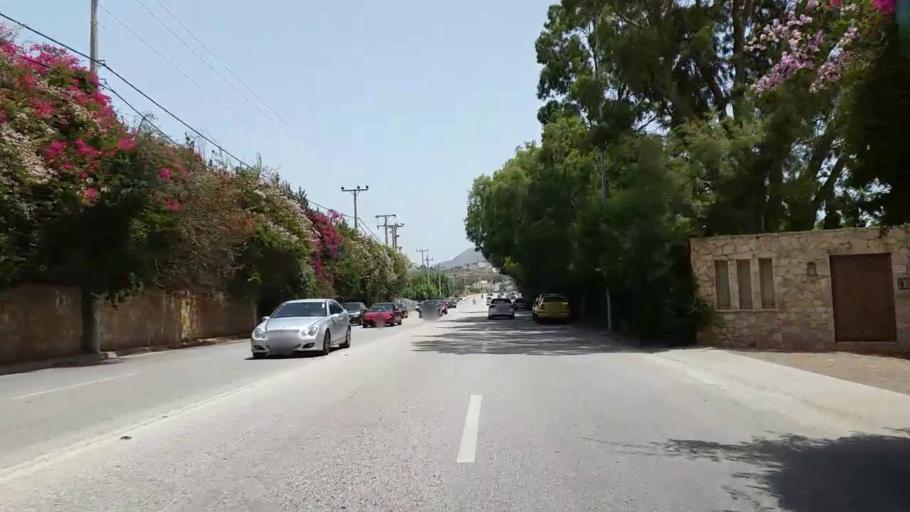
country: GR
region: Attica
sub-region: Nomarchia Anatolikis Attikis
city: Agios Dimitrios Kropias
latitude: 37.7940
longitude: 23.8755
